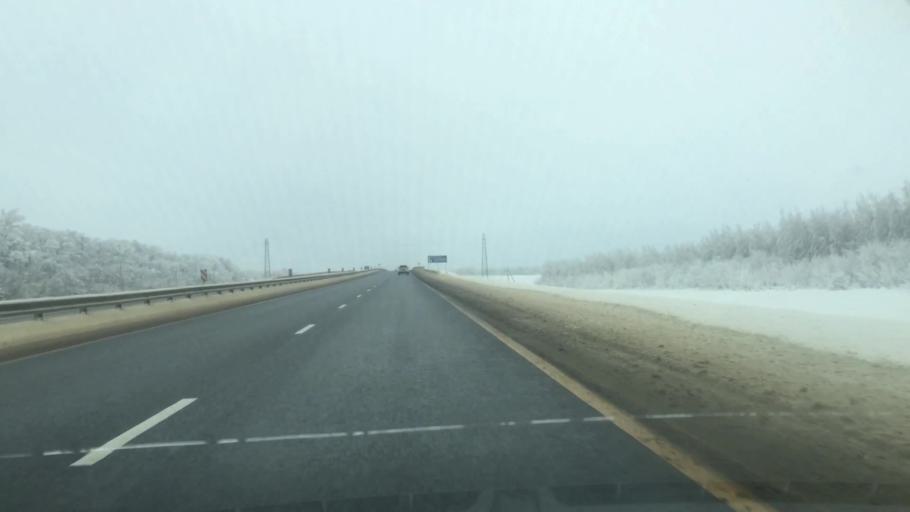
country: RU
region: Lipetsk
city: Zadonsk
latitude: 52.5086
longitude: 38.7557
